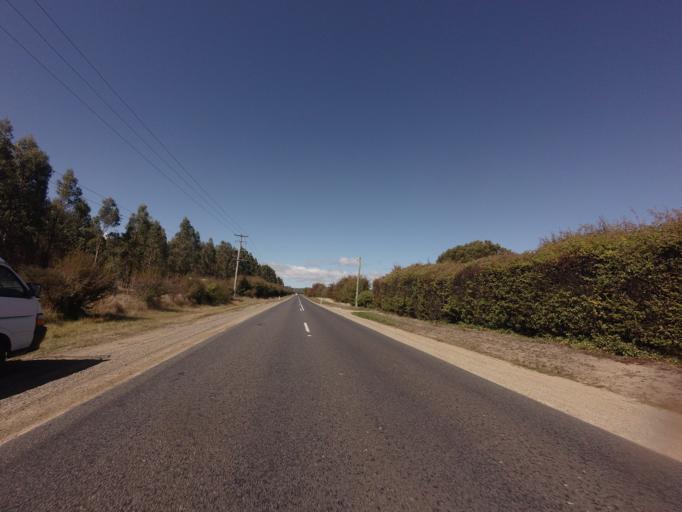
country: AU
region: Tasmania
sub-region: Break O'Day
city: St Helens
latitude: -41.5782
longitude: 148.1440
